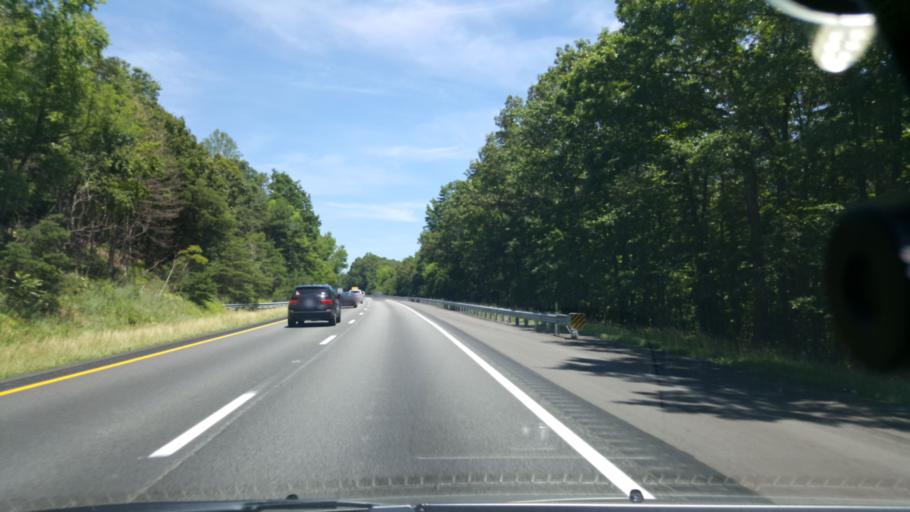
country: US
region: Virginia
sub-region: Botetourt County
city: Buchanan
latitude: 37.5315
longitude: -79.6886
